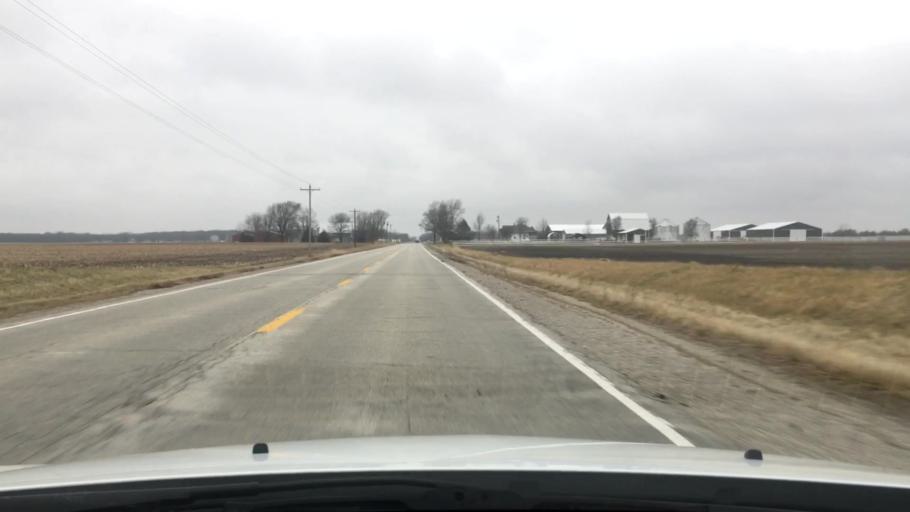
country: US
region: Illinois
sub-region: Iroquois County
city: Clifton
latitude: 40.8882
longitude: -87.8099
